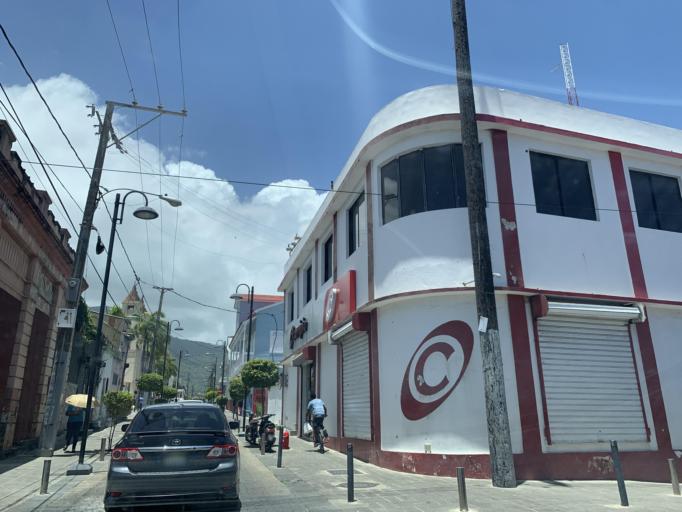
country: DO
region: Puerto Plata
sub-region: Puerto Plata
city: Puerto Plata
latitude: 19.7986
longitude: -70.6930
